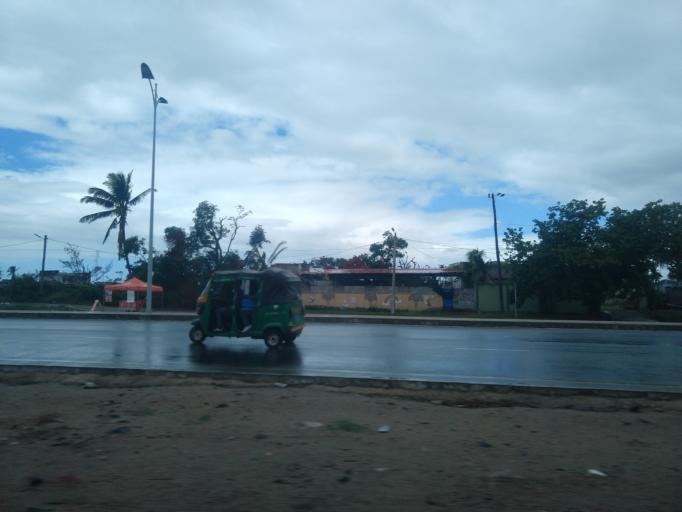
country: MZ
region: Sofala
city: Beira
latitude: -19.7841
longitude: 34.8771
